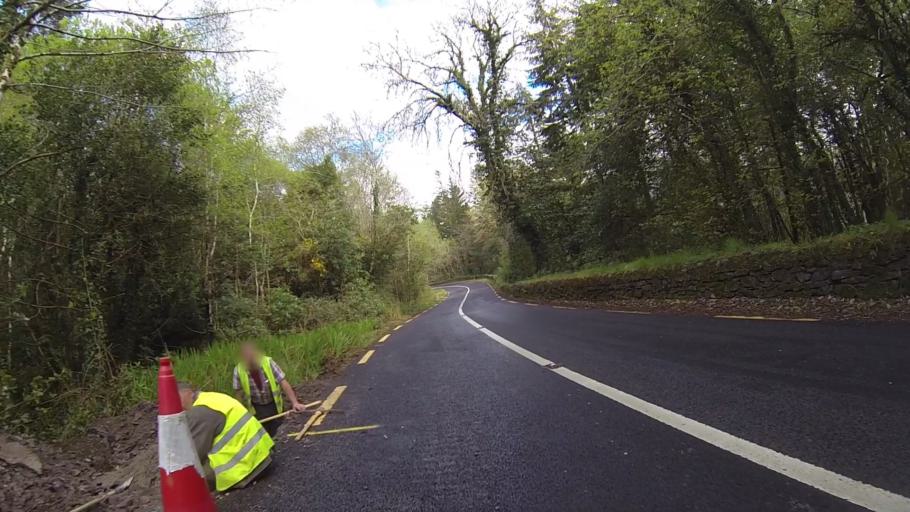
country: IE
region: Munster
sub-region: Ciarrai
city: Kenmare
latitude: 51.8193
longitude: -9.8680
